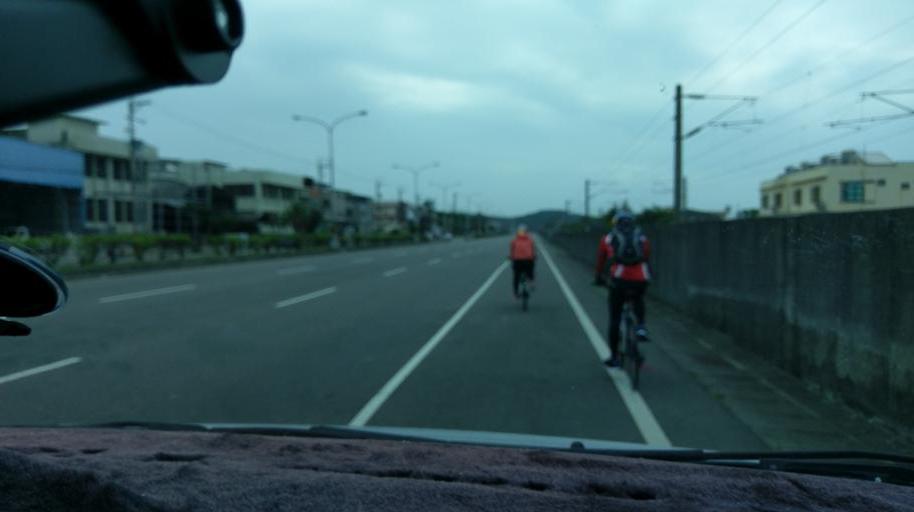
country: TW
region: Taiwan
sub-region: Miaoli
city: Miaoli
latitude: 24.5146
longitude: 120.6910
